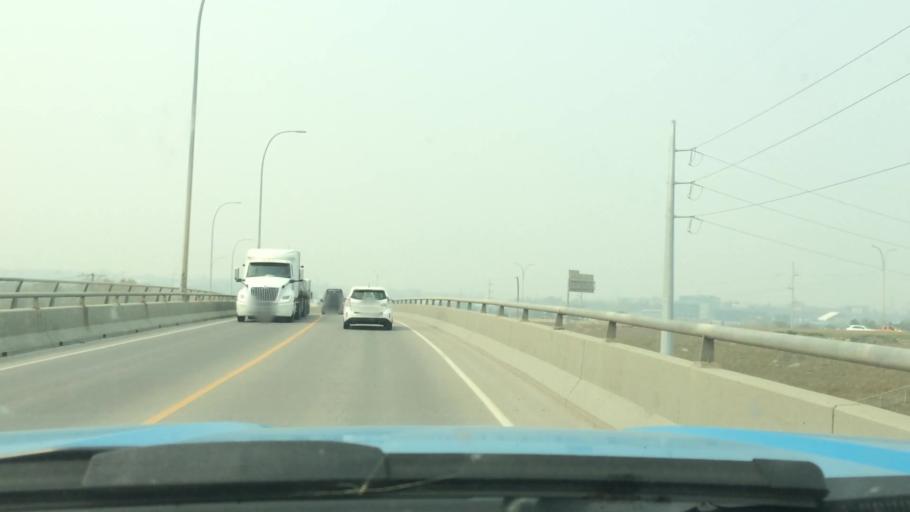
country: CA
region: Alberta
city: Calgary
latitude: 51.0088
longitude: -114.0103
